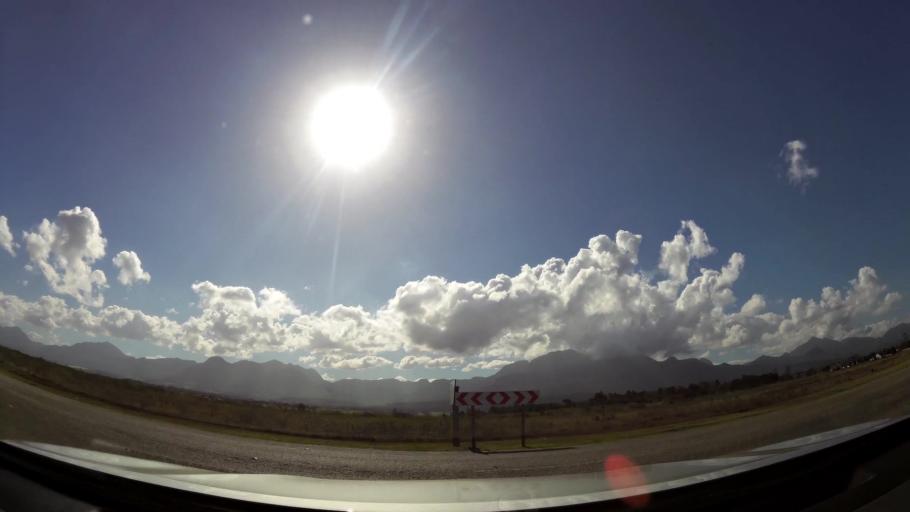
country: ZA
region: Western Cape
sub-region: Eden District Municipality
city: George
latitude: -33.9829
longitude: 22.4370
